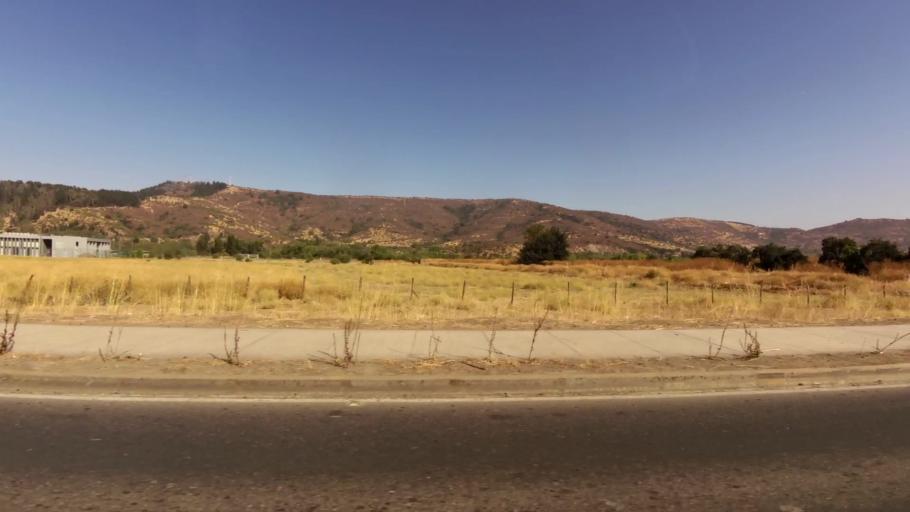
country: CL
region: Maule
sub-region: Provincia de Talca
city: Talca
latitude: -35.4146
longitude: -71.6728
